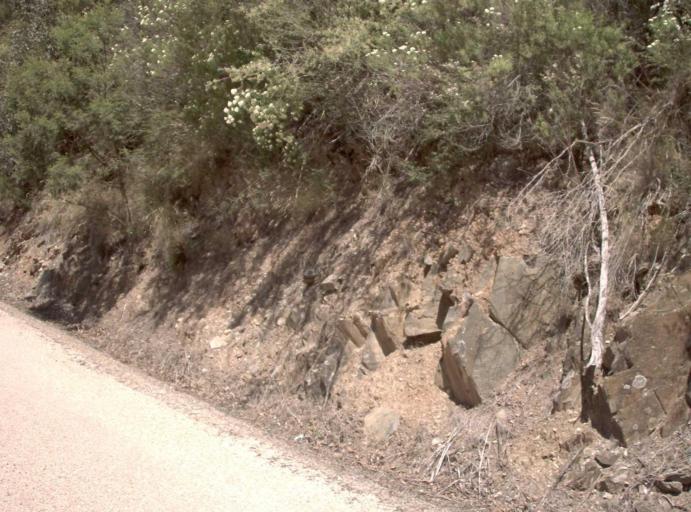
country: AU
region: Victoria
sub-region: East Gippsland
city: Bairnsdale
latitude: -37.4645
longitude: 147.8320
